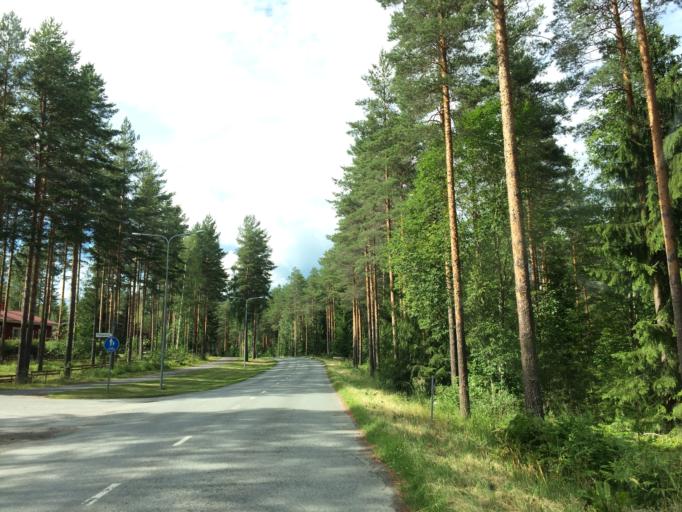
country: FI
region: Haeme
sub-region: Haemeenlinna
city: Turenki
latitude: 60.9378
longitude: 24.6486
